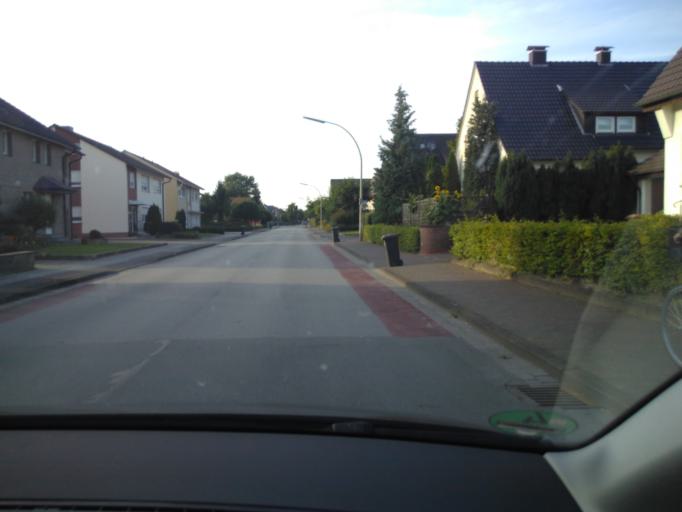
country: DE
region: North Rhine-Westphalia
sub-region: Regierungsbezirk Detmold
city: Rheda-Wiedenbruck
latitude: 51.8479
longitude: 8.2792
